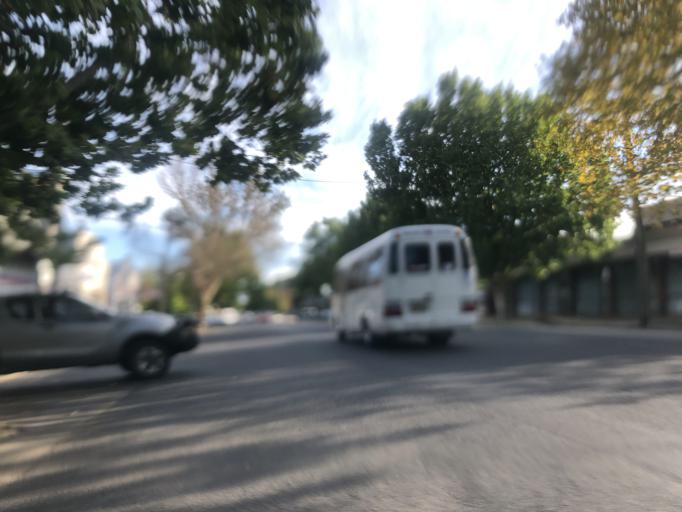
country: AU
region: New South Wales
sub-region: Orange Municipality
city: Orange
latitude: -33.2870
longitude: 149.1004
